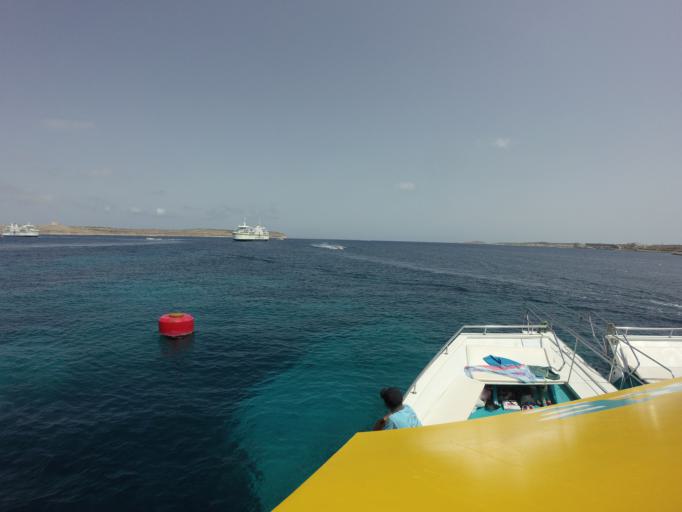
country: MT
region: Il-Mellieha
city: Mellieha
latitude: 35.9888
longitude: 14.3305
